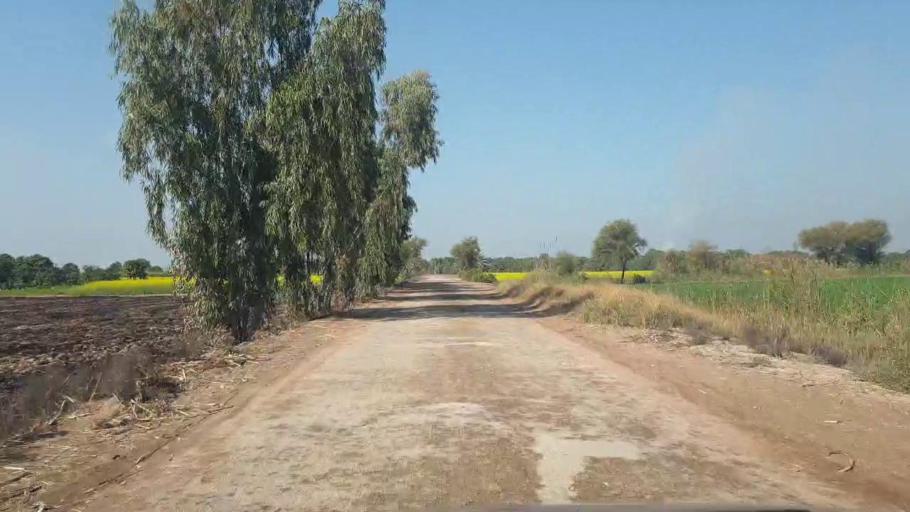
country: PK
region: Sindh
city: Shahdadpur
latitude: 25.9120
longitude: 68.5941
